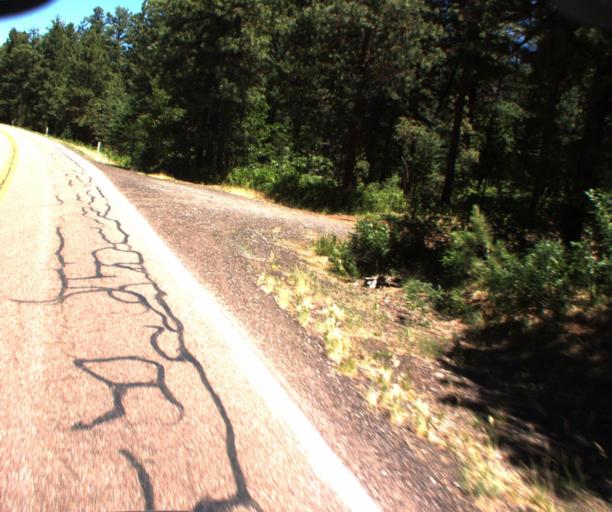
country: US
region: Arizona
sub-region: Gila County
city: Pine
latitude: 34.4646
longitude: -111.3841
